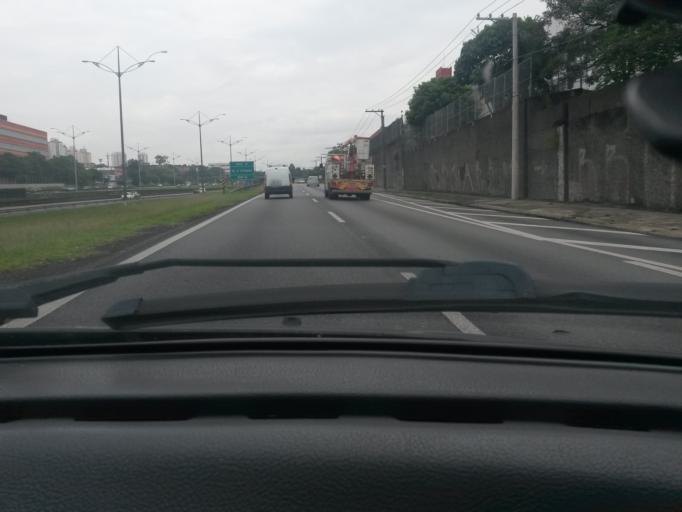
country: BR
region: Sao Paulo
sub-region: Sao Caetano Do Sul
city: Sao Caetano do Sul
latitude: -23.6354
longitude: -46.5949
